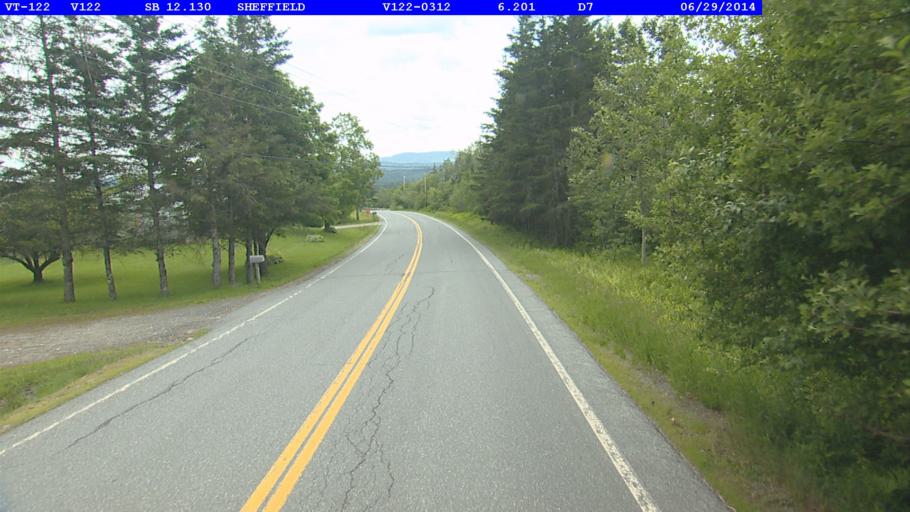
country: US
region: Vermont
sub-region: Caledonia County
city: Lyndonville
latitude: 44.6577
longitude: -72.1626
